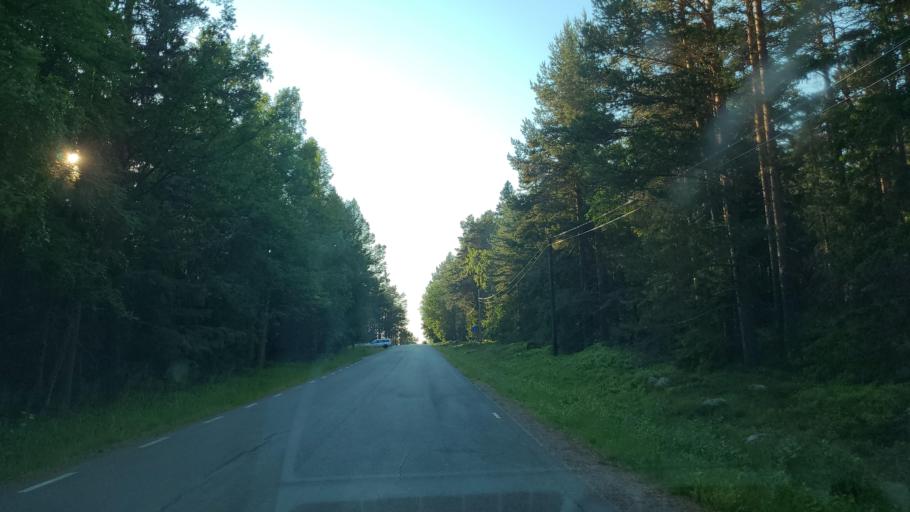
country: SE
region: Vaesterbotten
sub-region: Skelleftea Kommun
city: Skelleftehamn
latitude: 64.4745
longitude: 21.5782
